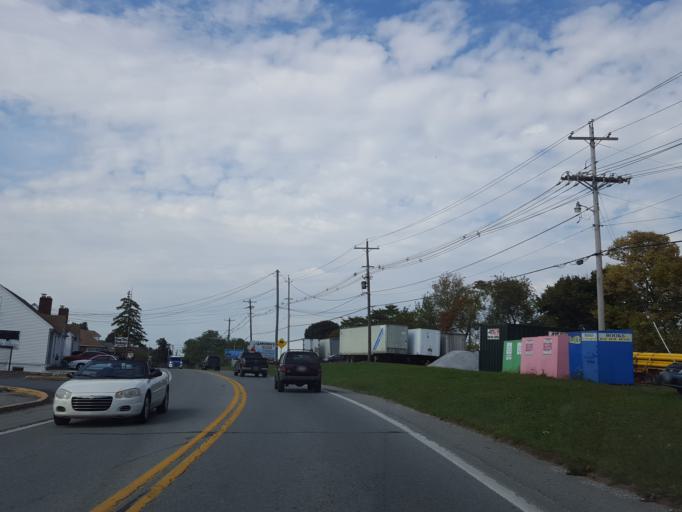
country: US
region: Pennsylvania
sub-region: York County
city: Dallastown
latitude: 39.9066
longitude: -76.6542
